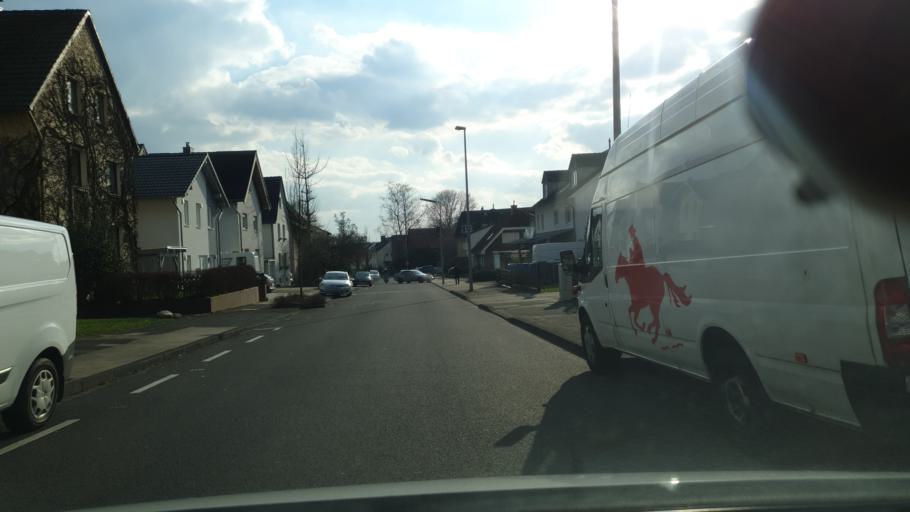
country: DE
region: North Rhine-Westphalia
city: Opladen
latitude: 51.0486
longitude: 7.0534
